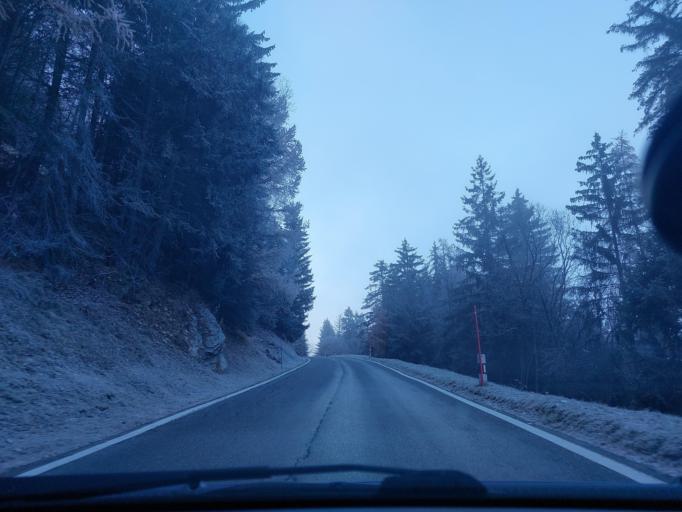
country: CH
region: Valais
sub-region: Conthey District
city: Basse-Nendaz
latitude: 46.1439
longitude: 7.3161
